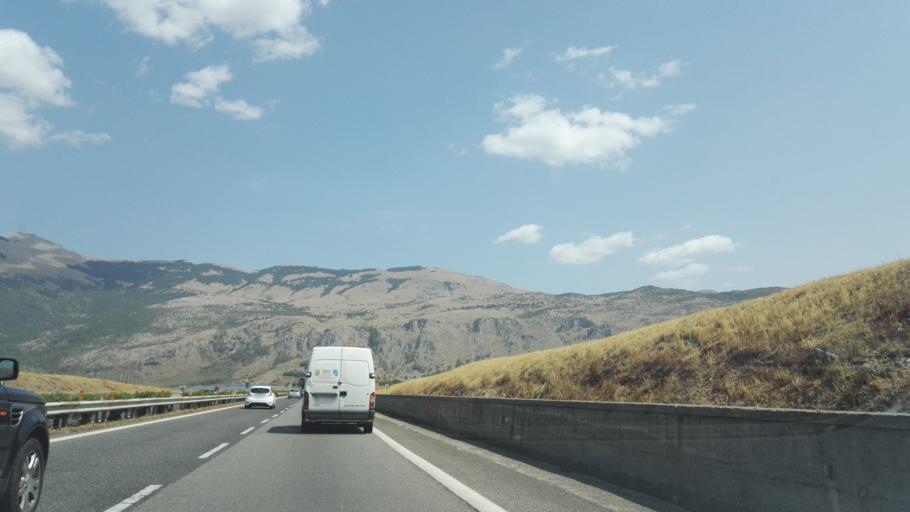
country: IT
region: Calabria
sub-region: Provincia di Cosenza
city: Frascineto
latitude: 39.8159
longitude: 16.2542
